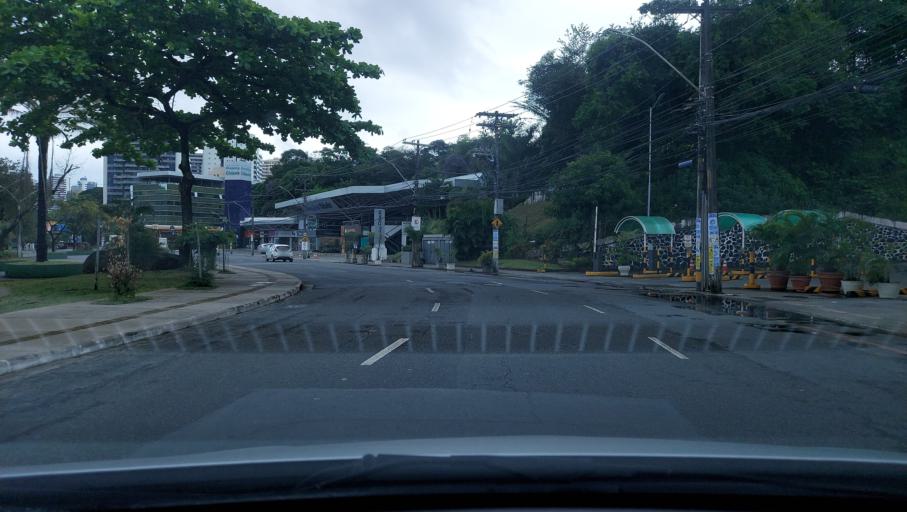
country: BR
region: Bahia
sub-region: Salvador
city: Salvador
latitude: -12.9960
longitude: -38.4682
